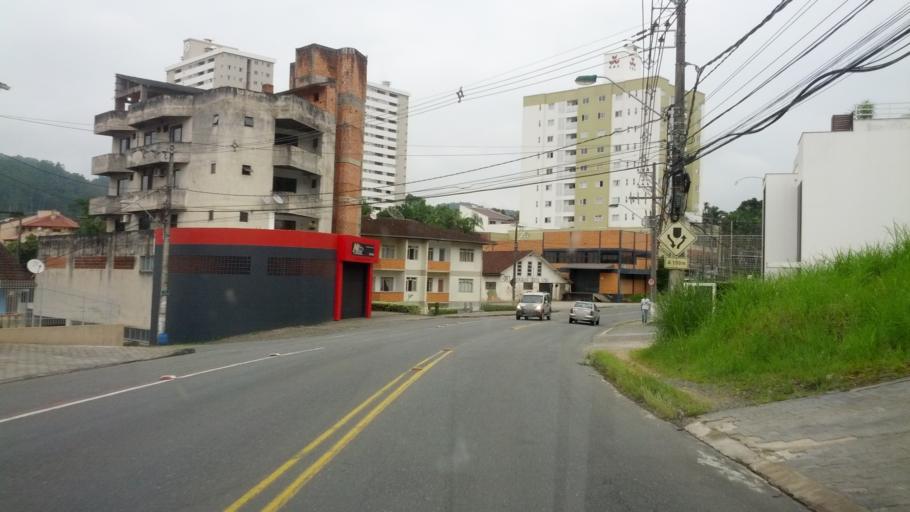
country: BR
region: Santa Catarina
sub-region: Blumenau
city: Blumenau
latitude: -26.9180
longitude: -49.1157
